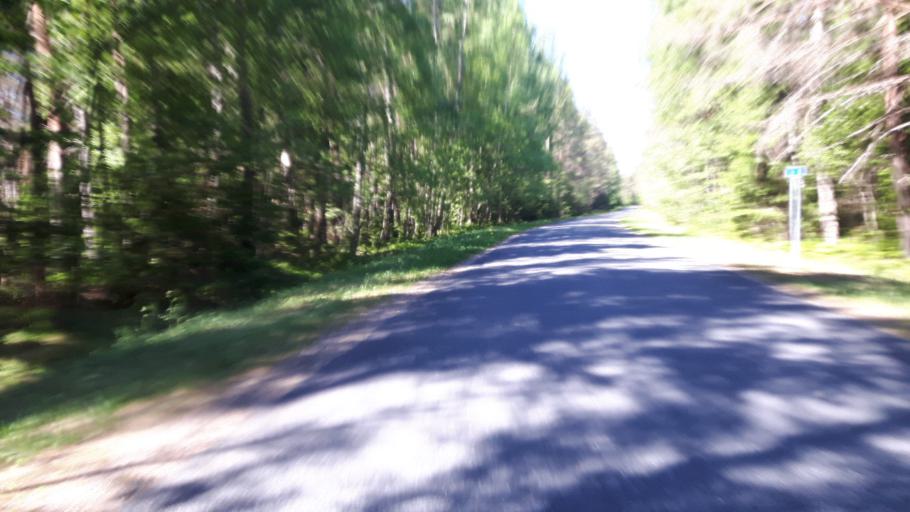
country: EE
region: Harju
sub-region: Loksa linn
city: Loksa
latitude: 59.5718
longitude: 25.6191
